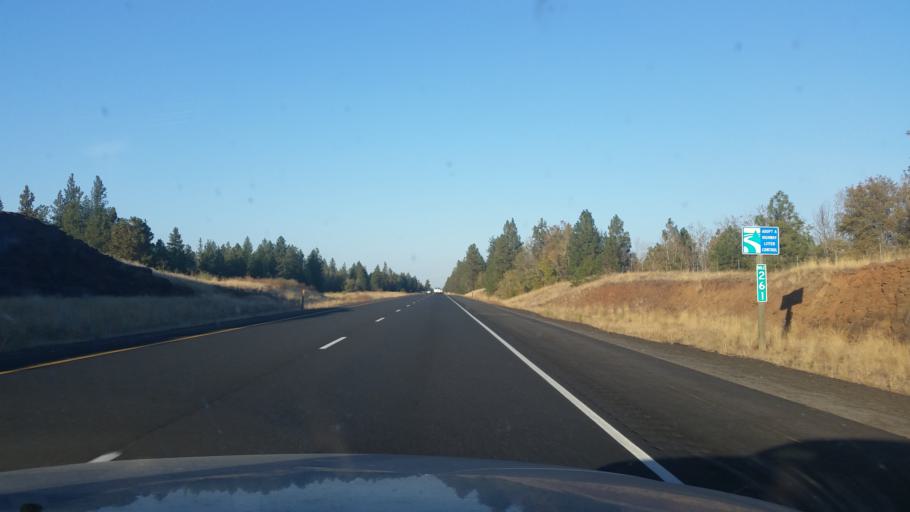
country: US
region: Washington
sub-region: Spokane County
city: Medical Lake
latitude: 47.4698
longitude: -117.7411
